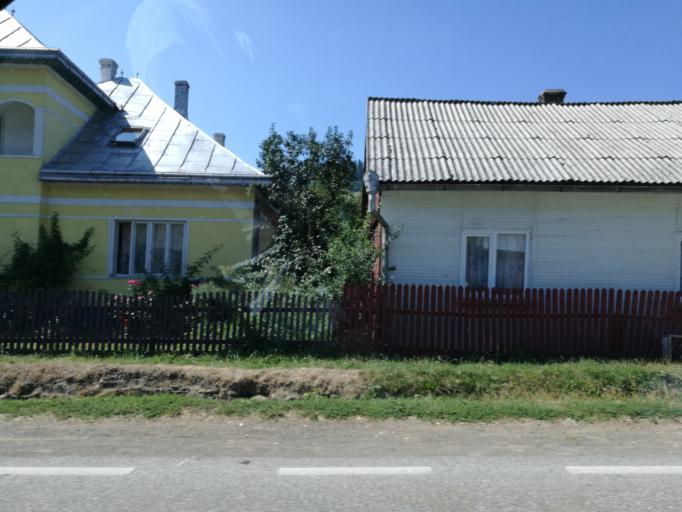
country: RO
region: Suceava
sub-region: Comuna Putna
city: Putna
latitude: 47.8725
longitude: 25.6141
